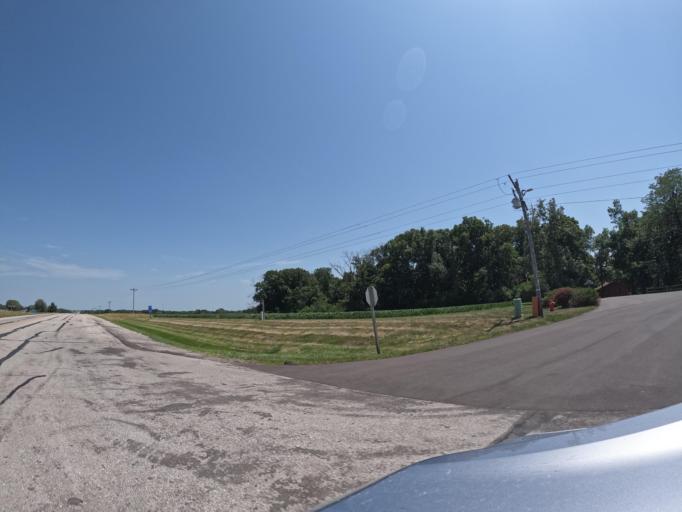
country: US
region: Iowa
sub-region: Henry County
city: Mount Pleasant
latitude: 40.9671
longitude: -91.6221
